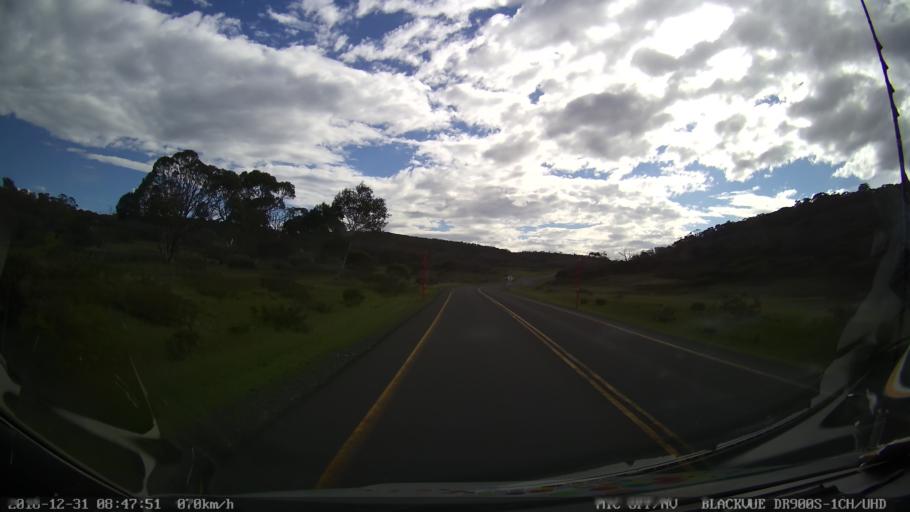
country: AU
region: New South Wales
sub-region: Snowy River
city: Jindabyne
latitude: -36.3601
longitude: 148.4891
